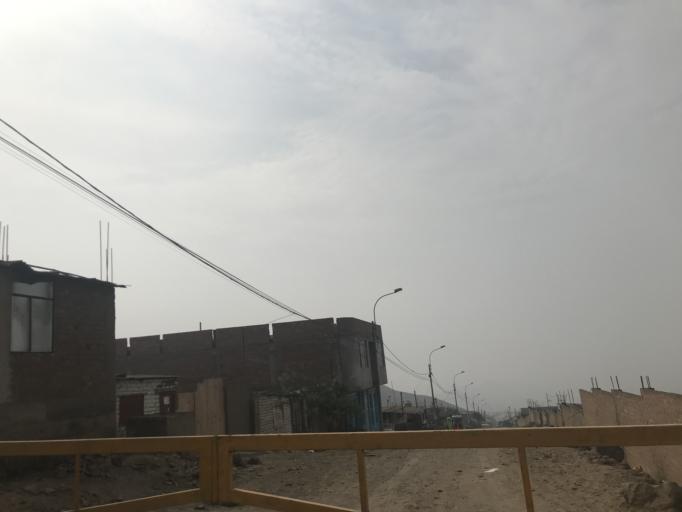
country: PE
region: Lima
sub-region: Lima
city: Carabayllo
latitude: -11.8178
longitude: -77.0443
